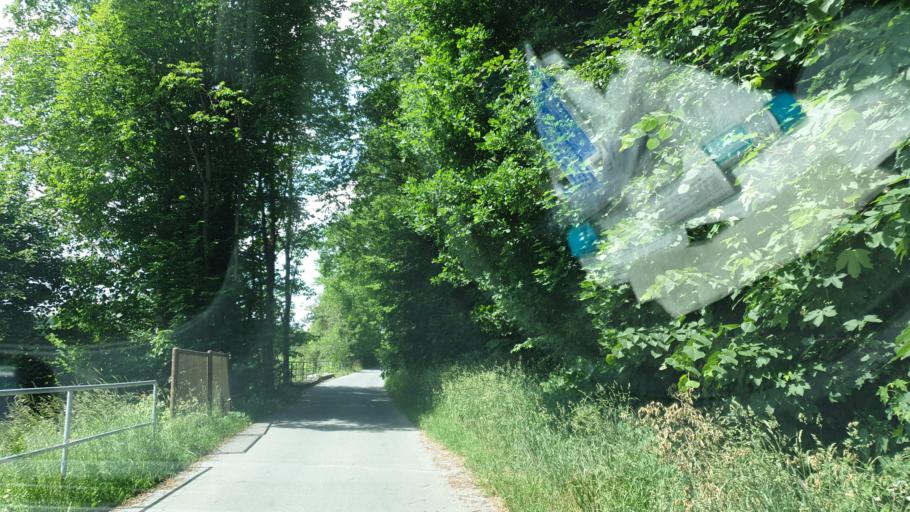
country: DE
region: Saxony
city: Adorf
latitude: 50.3243
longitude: 12.2621
